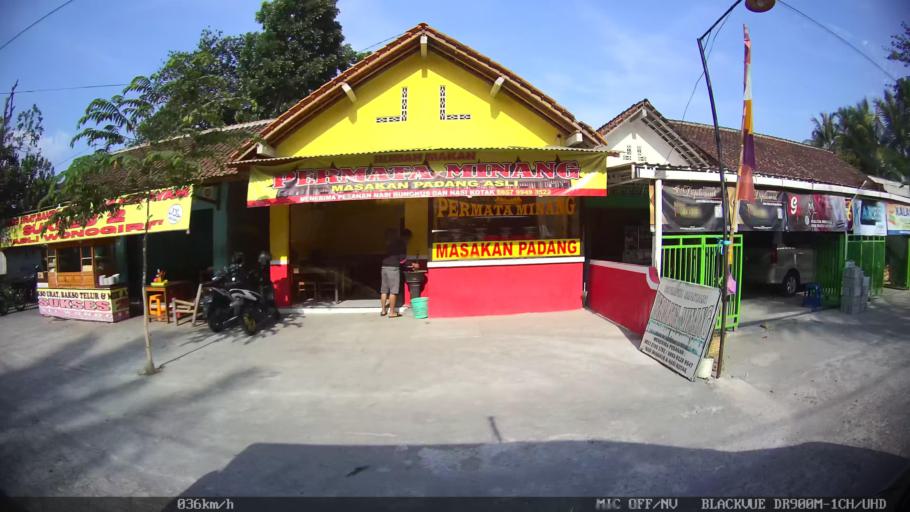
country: ID
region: Daerah Istimewa Yogyakarta
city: Bantul
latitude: -7.8880
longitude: 110.3039
